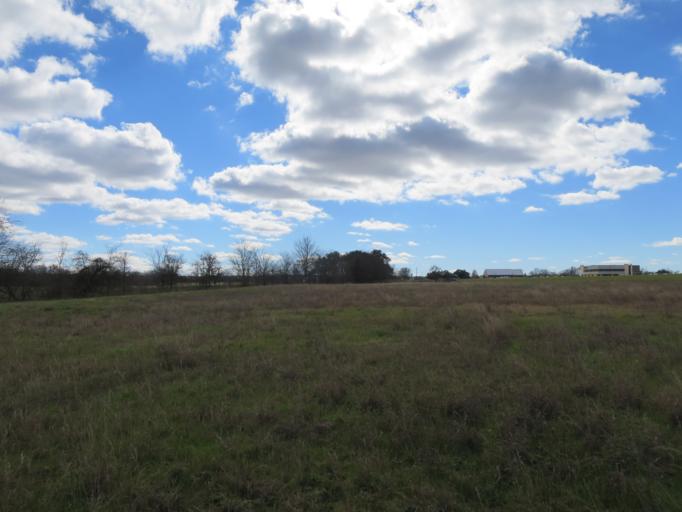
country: US
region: Texas
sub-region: Williamson County
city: Round Rock
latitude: 30.5321
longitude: -97.6252
